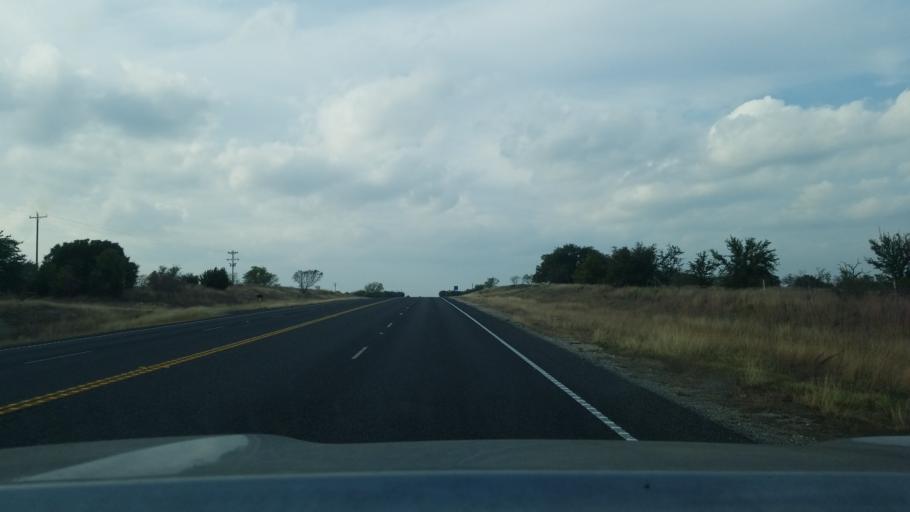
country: US
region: Texas
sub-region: Mills County
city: Goldthwaite
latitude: 31.3651
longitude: -98.5164
